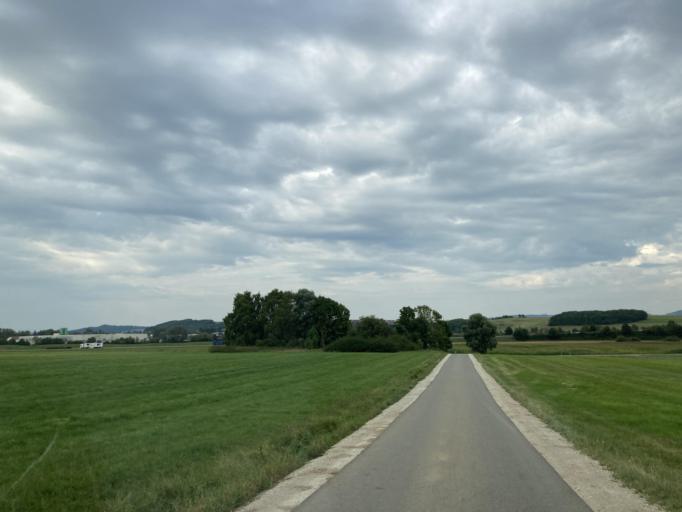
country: DE
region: Baden-Wuerttemberg
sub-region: Freiburg Region
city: Hufingen
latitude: 47.9235
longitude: 8.5466
